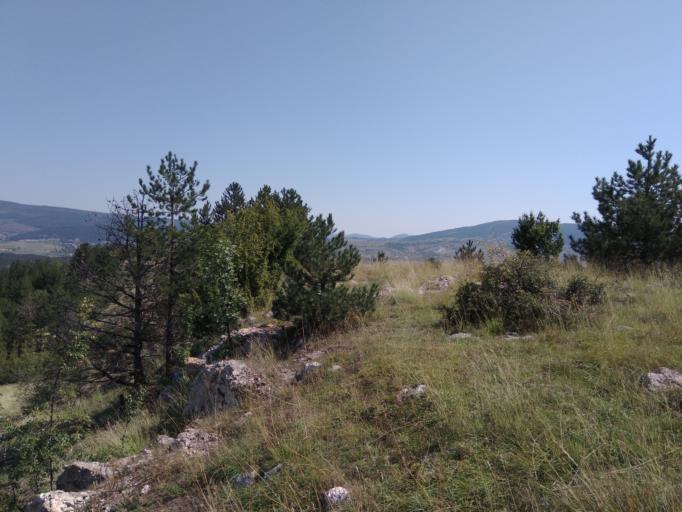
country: BG
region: Kurdzhali
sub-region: Obshtina Kurdzhali
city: Kurdzhali
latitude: 41.6349
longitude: 25.4536
